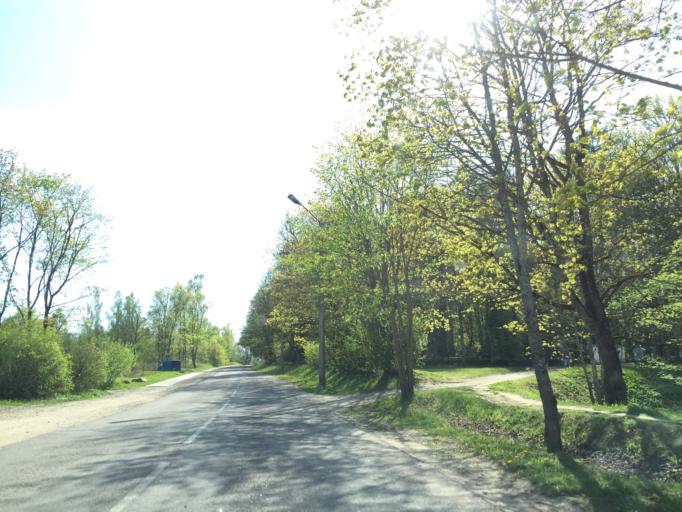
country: LV
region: Limbazu Rajons
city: Limbazi
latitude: 57.5090
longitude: 24.6970
